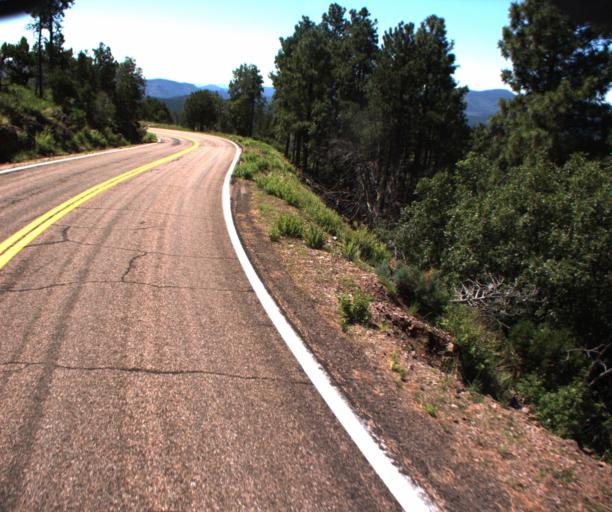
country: US
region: Arizona
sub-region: Greenlee County
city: Morenci
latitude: 33.5540
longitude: -109.3219
